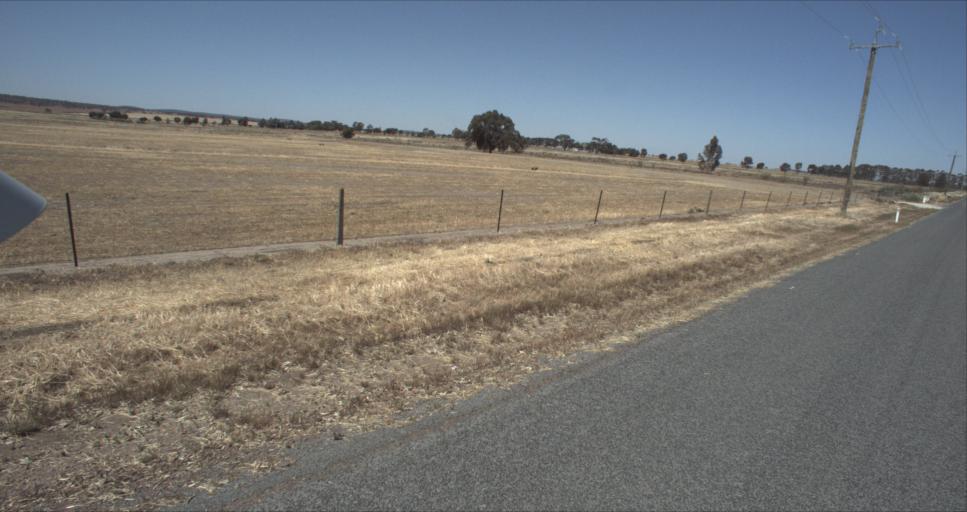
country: AU
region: New South Wales
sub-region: Leeton
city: Leeton
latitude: -34.5298
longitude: 146.4454
